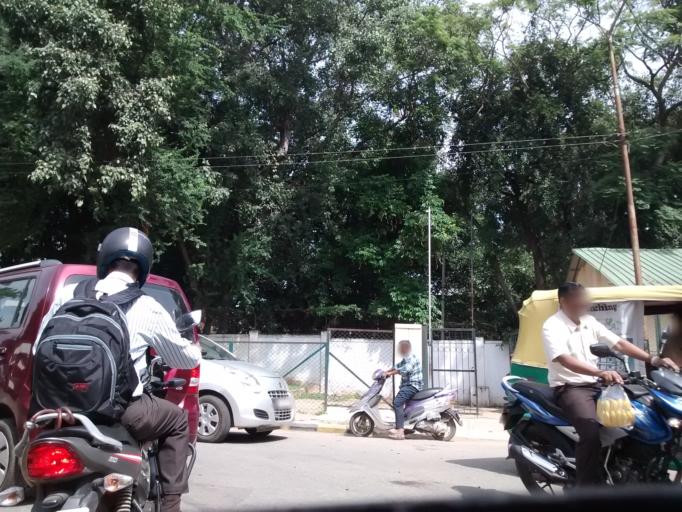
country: IN
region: Karnataka
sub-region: Bangalore Urban
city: Bangalore
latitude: 12.9640
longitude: 77.6654
